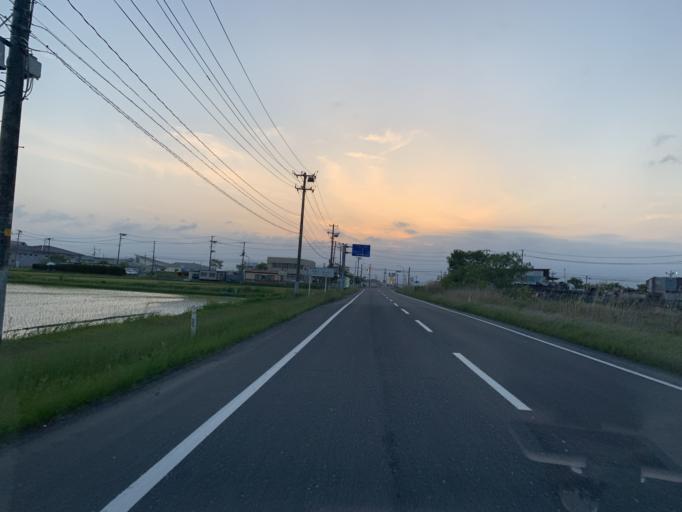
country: JP
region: Iwate
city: Ichinoseki
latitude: 38.8017
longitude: 141.0703
